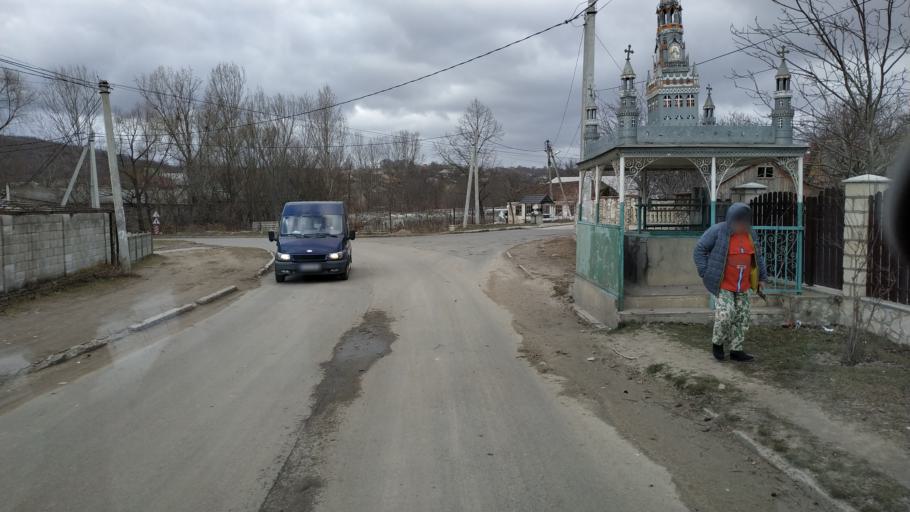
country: MD
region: Stinga Nistrului
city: Bucovat
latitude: 47.2311
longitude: 28.4283
